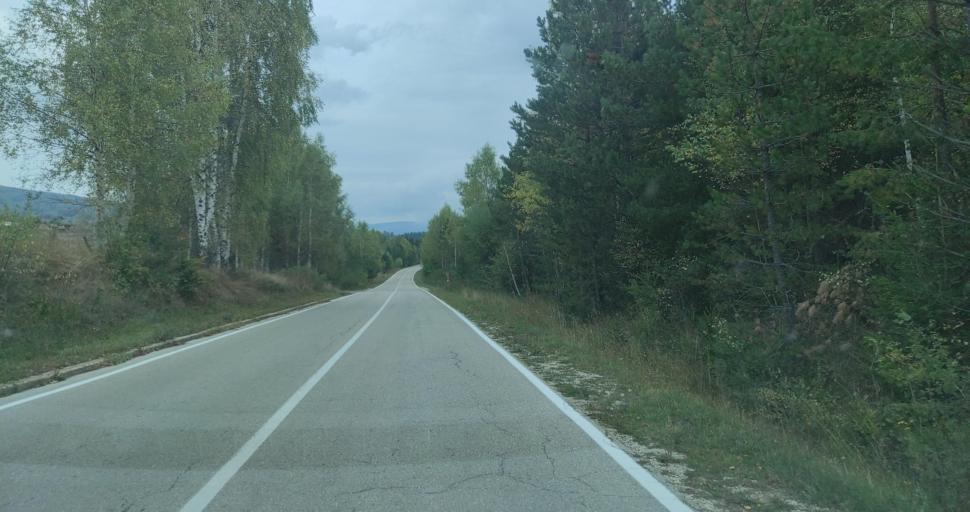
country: RS
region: Central Serbia
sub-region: Jablanicki Okrug
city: Crna Trava
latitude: 42.6881
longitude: 22.3164
